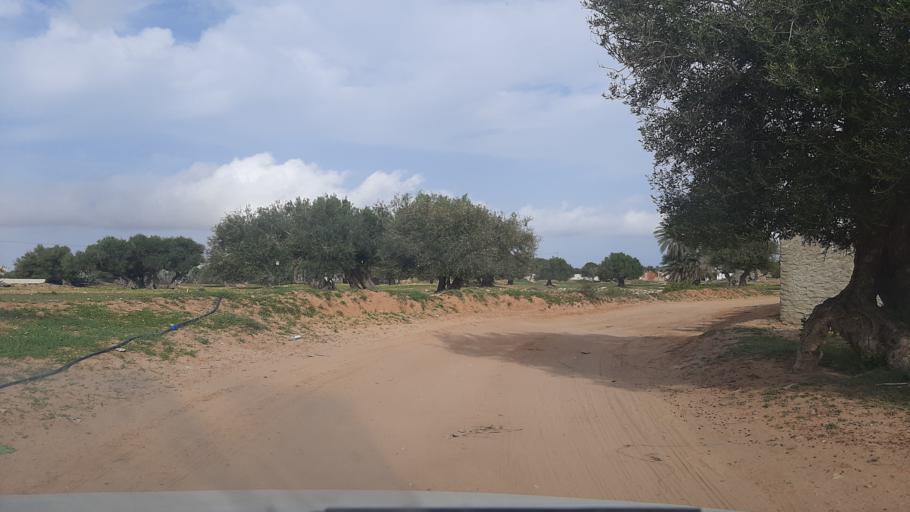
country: TN
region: Madanin
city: Midoun
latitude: 33.8075
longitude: 11.0236
